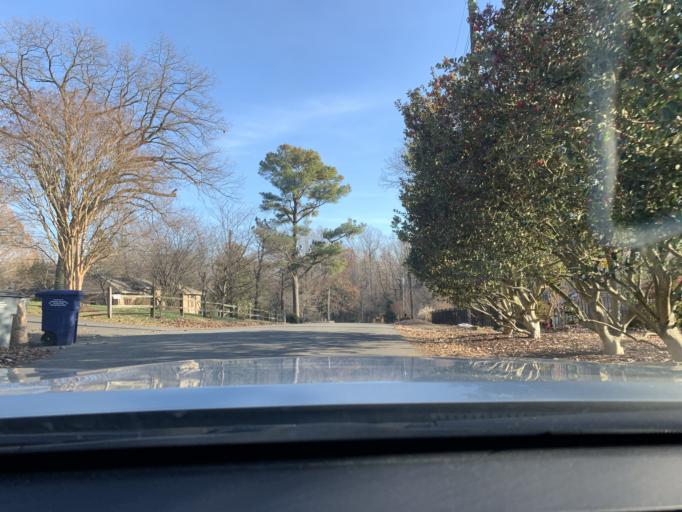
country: US
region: Virginia
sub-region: Fairfax County
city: Seven Corners
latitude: 38.8607
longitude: -77.1625
